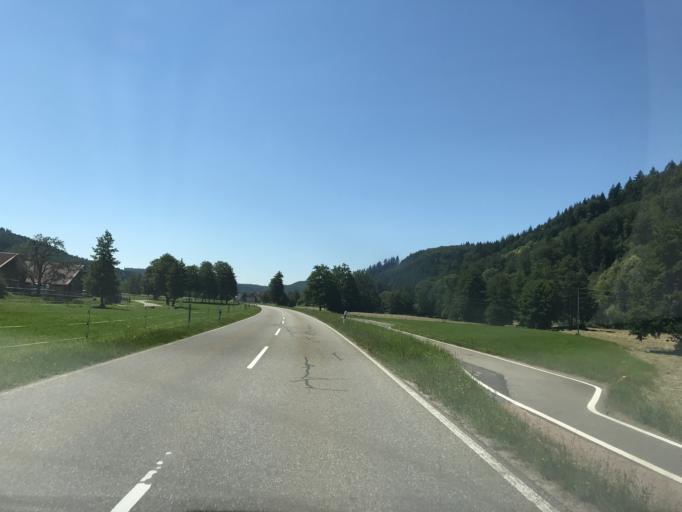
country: DE
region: Baden-Wuerttemberg
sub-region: Freiburg Region
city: Schopfheim
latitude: 47.6701
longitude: 7.8023
